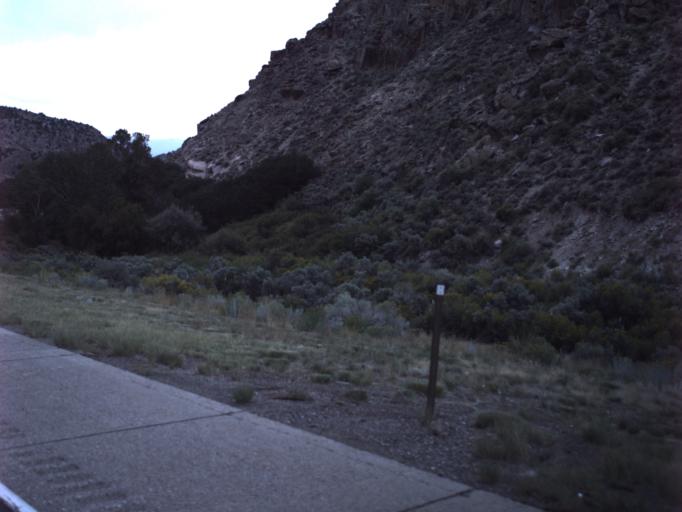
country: US
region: Utah
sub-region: Sevier County
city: Monroe
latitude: 38.5776
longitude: -112.3304
